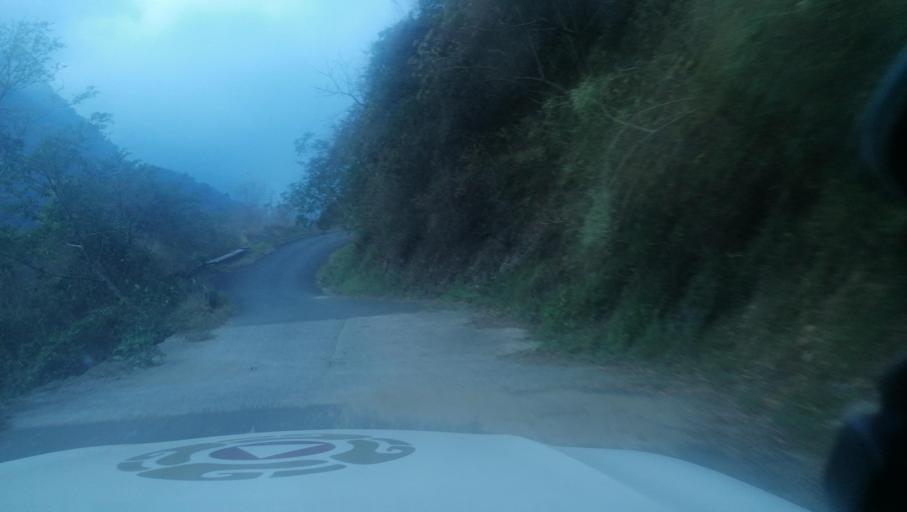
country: MX
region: Chiapas
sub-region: Cacahoatan
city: Benito Juarez
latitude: 15.1391
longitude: -92.1980
